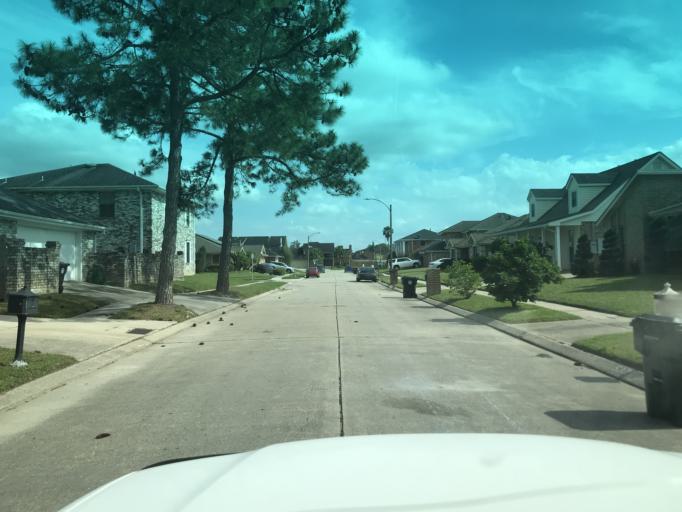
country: US
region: Louisiana
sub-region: Saint Bernard Parish
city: Chalmette
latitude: 30.0332
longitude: -89.9548
